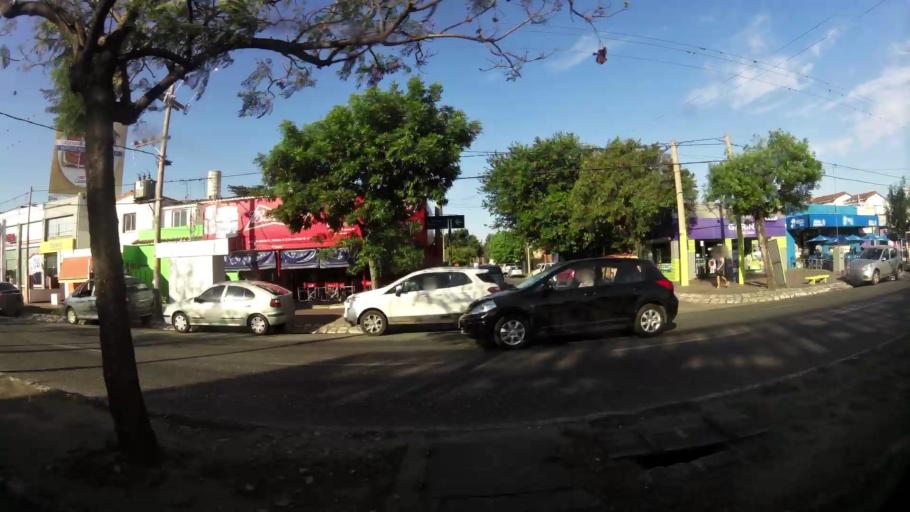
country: AR
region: Cordoba
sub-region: Departamento de Capital
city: Cordoba
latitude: -31.3750
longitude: -64.2275
